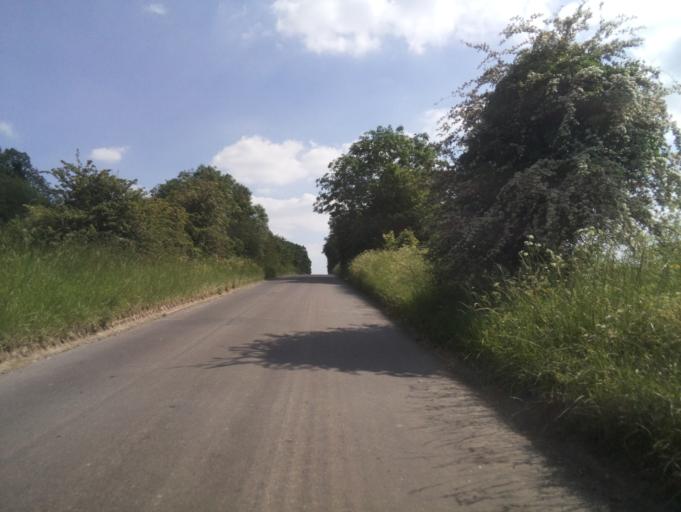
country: GB
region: England
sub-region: Wiltshire
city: Collingbourne Kingston
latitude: 51.2786
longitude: -1.7089
